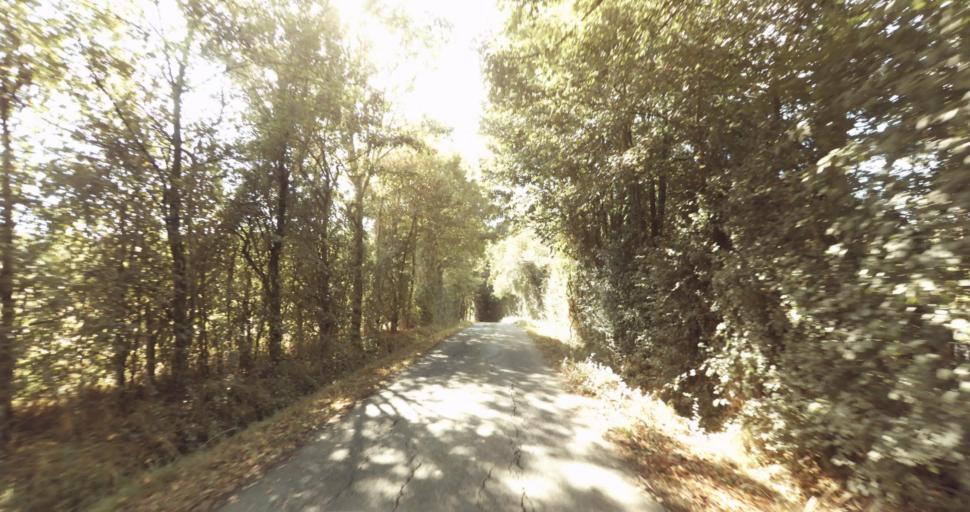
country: FR
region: Lower Normandy
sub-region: Departement de l'Orne
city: Vimoutiers
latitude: 48.9187
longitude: 0.1335
